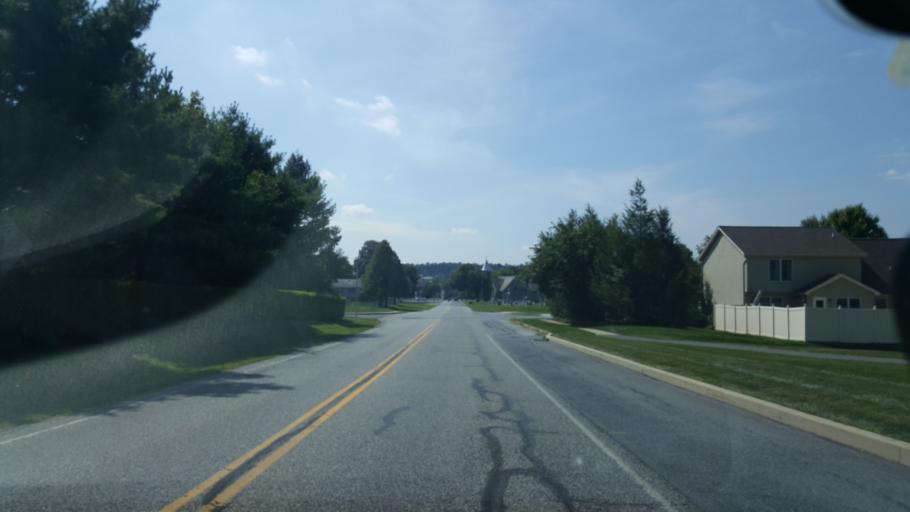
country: US
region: Pennsylvania
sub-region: Lebanon County
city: Campbelltown
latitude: 40.2806
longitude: -76.5761
